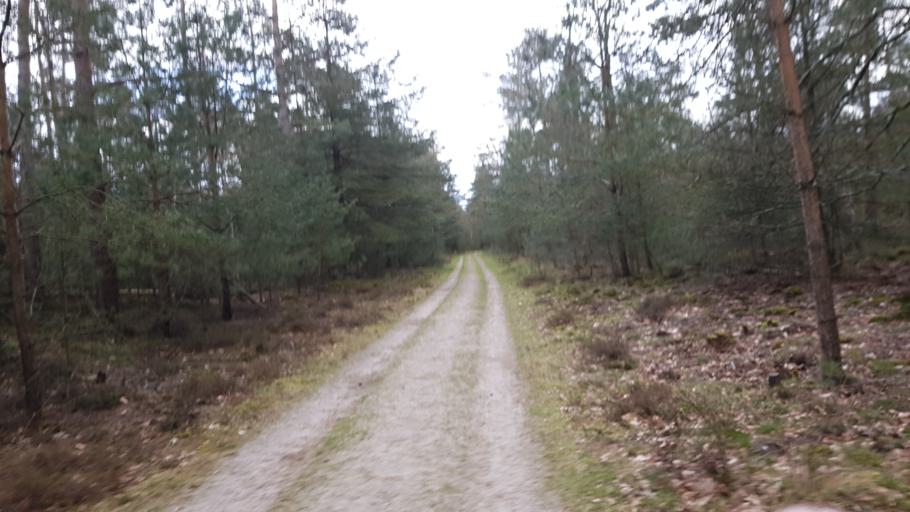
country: NL
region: Gelderland
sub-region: Gemeente Epe
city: Vaassen
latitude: 52.3080
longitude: 5.9229
